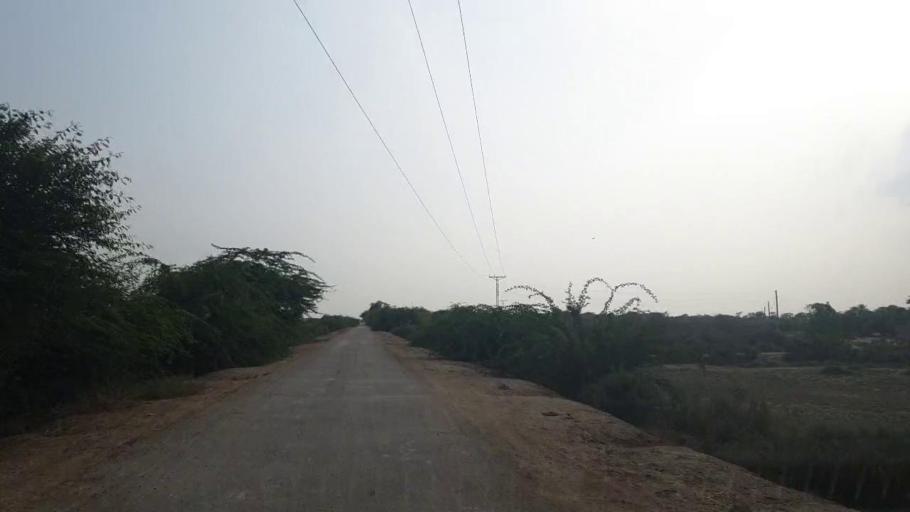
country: PK
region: Sindh
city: Badin
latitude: 24.6367
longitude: 68.6926
